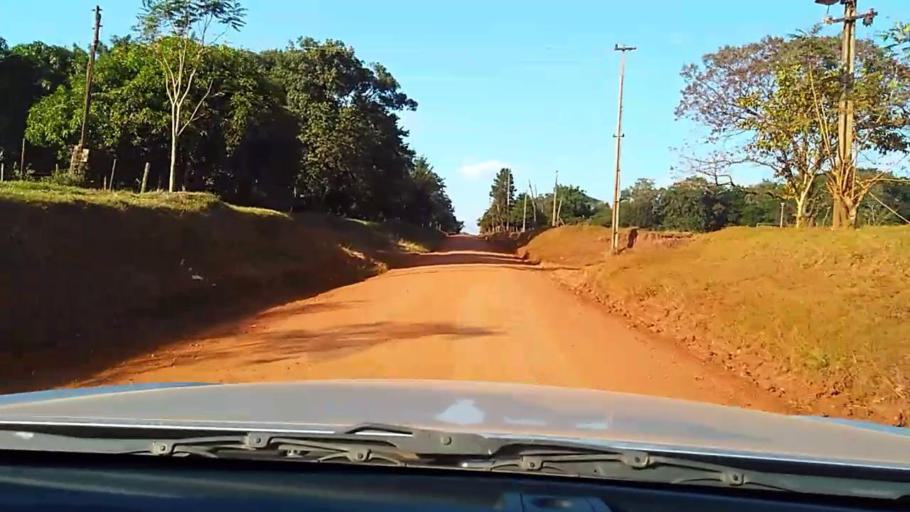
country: PY
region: Alto Parana
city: Doctor Juan Leon Mallorquin
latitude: -25.6897
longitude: -55.3775
